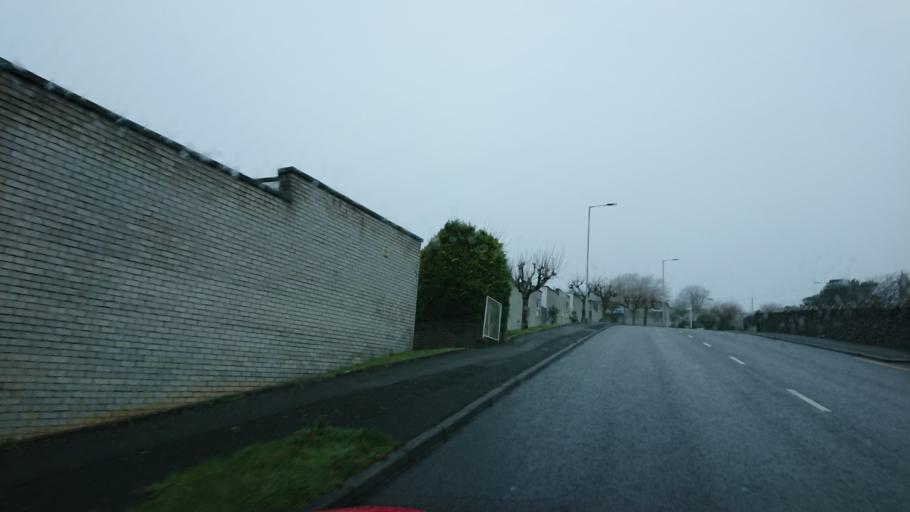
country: GB
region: England
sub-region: Plymouth
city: Plymstock
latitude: 50.3539
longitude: -4.1160
